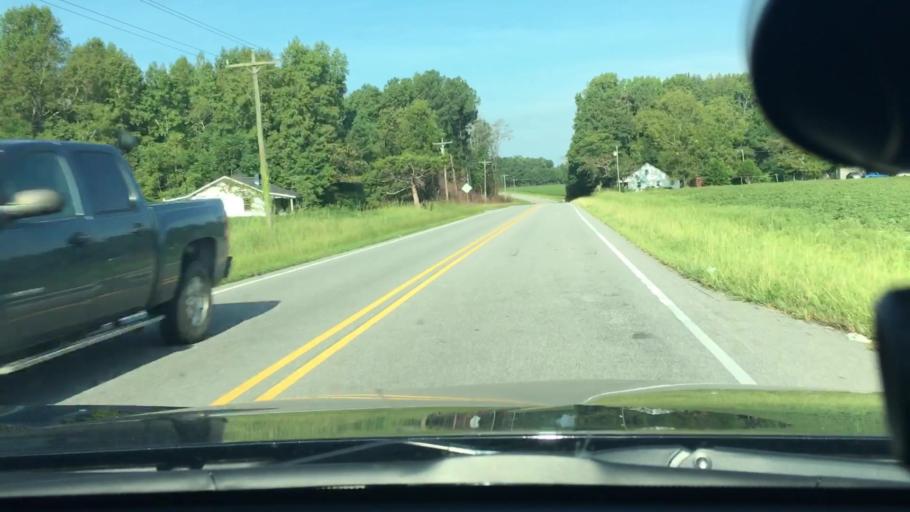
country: US
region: North Carolina
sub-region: Edgecombe County
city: Pinetops
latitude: 35.7795
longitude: -77.5955
